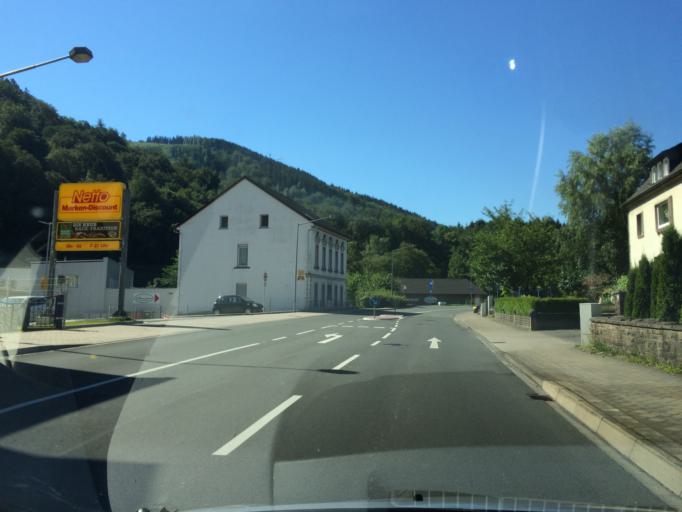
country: DE
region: North Rhine-Westphalia
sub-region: Regierungsbezirk Arnsberg
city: Nachrodt-Wiblingwerde
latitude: 51.3324
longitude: 7.6523
